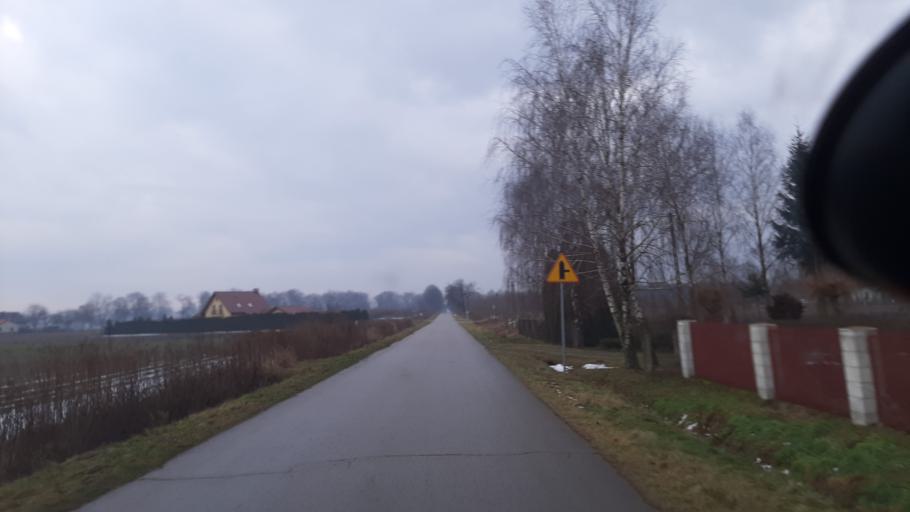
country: PL
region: Lublin Voivodeship
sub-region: Powiat lubelski
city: Lublin
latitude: 51.3368
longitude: 22.5451
